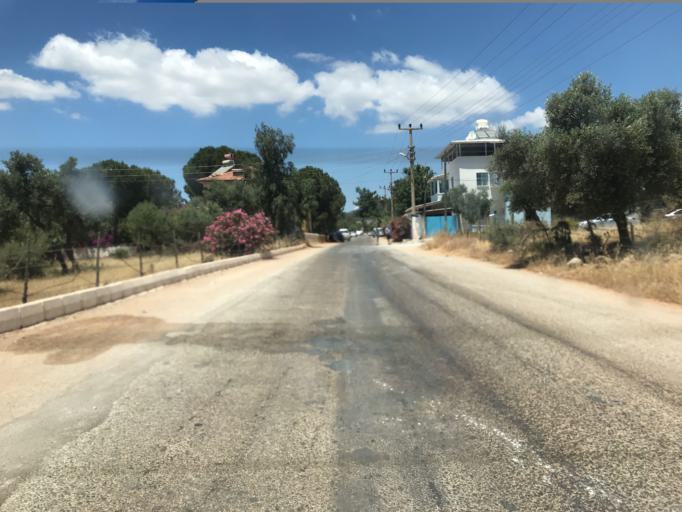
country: TR
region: Aydin
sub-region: Didim
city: Didim
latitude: 37.4049
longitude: 27.4283
